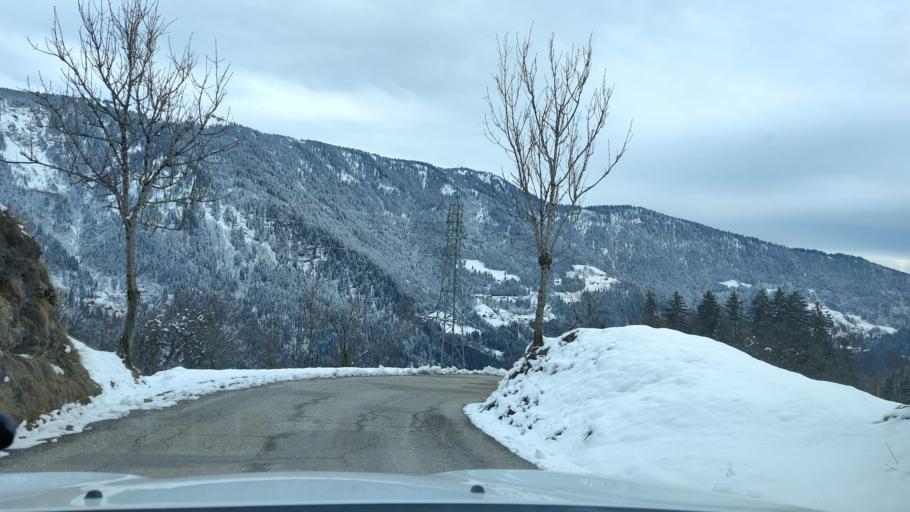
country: FR
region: Rhone-Alpes
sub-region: Departement de la Savoie
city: Ugine
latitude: 45.7783
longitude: 6.4761
